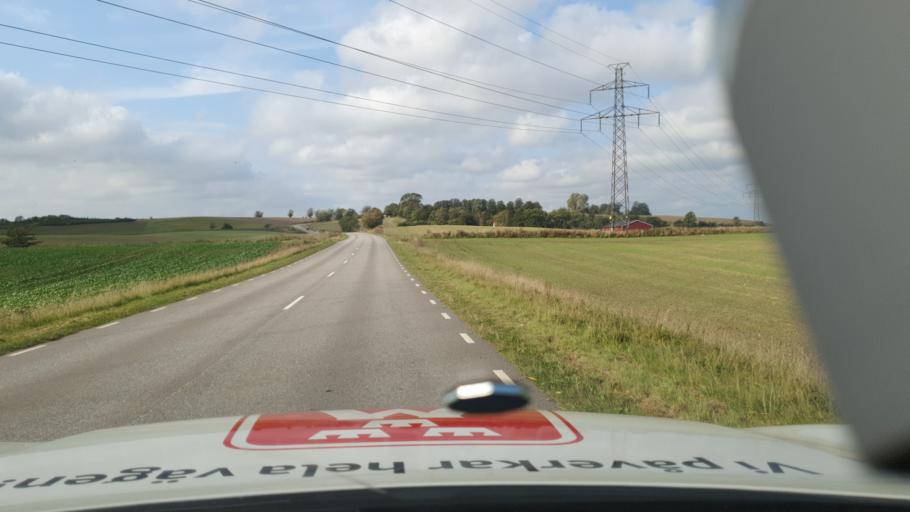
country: SE
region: Skane
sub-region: Svedala Kommun
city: Svedala
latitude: 55.4966
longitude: 13.1737
